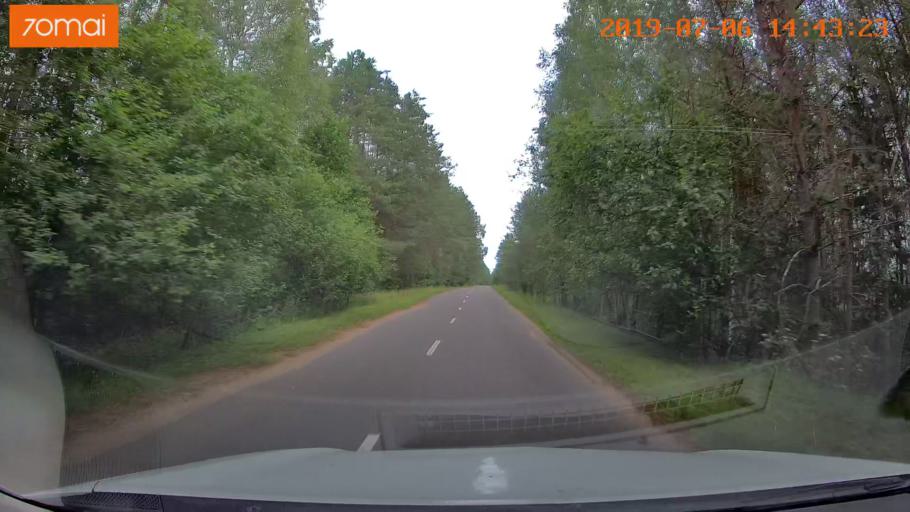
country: BY
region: Minsk
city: Ivyanyets
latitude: 53.9512
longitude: 26.6936
